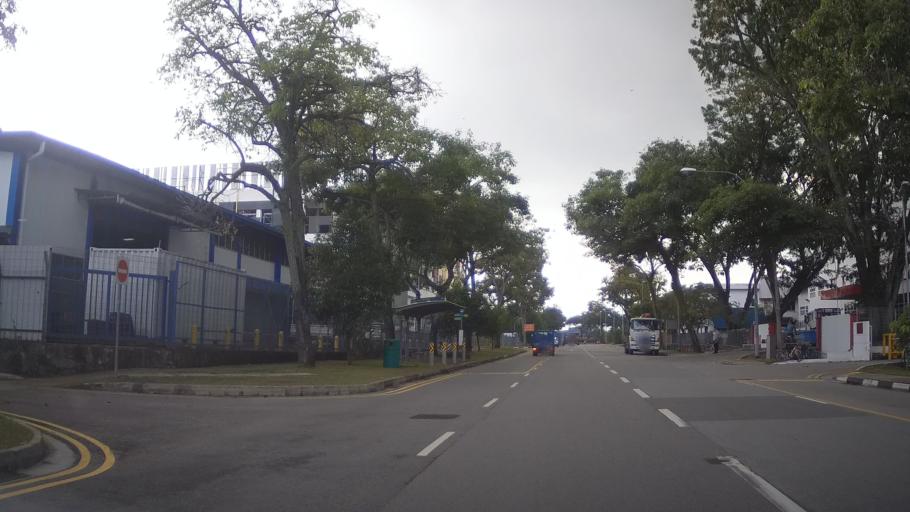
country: MY
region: Johor
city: Johor Bahru
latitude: 1.3258
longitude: 103.6838
